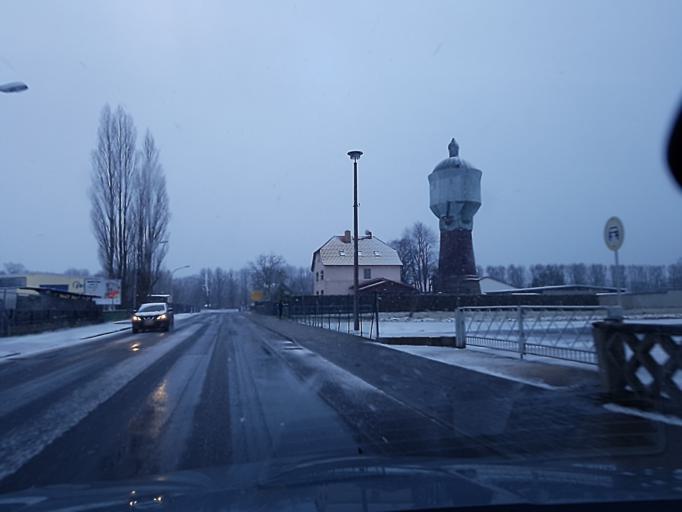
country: DE
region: Brandenburg
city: Elsterwerda
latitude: 51.4560
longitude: 13.5183
